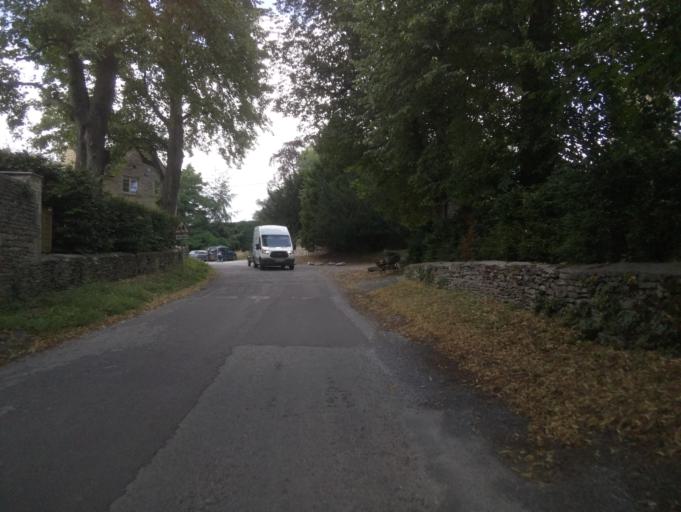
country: GB
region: England
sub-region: Wiltshire
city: Hankerton
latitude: 51.6344
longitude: -2.0647
